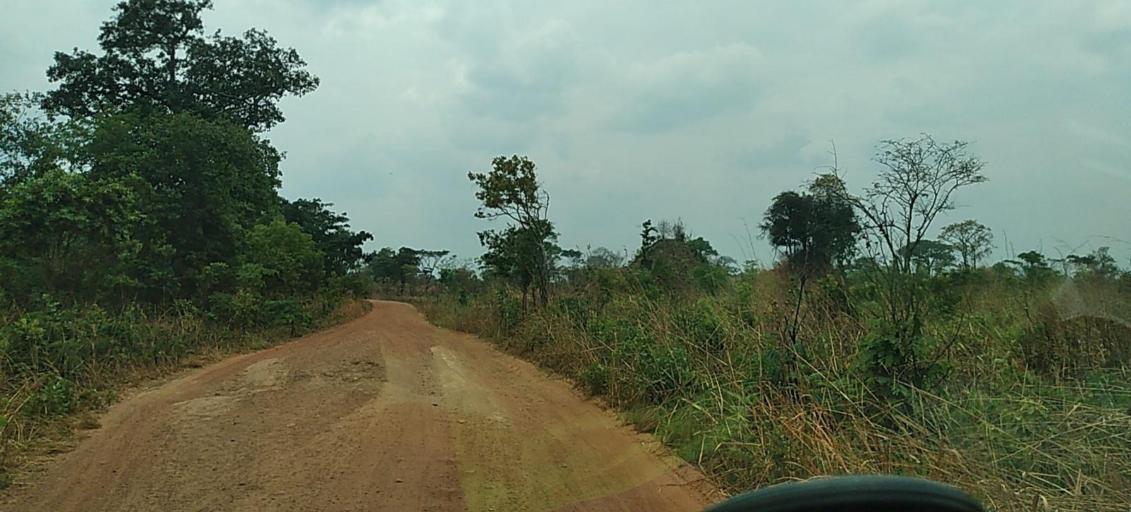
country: ZM
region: North-Western
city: Kansanshi
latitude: -12.0779
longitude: 26.3581
